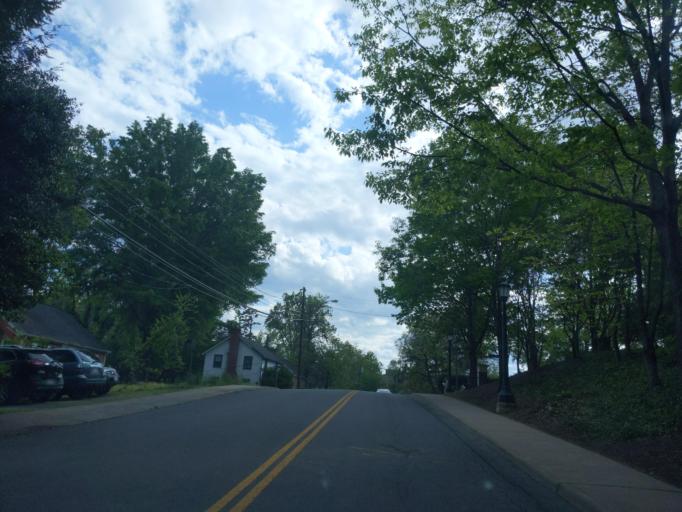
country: US
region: Virginia
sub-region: City of Charlottesville
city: Charlottesville
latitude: 38.0294
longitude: -78.5134
